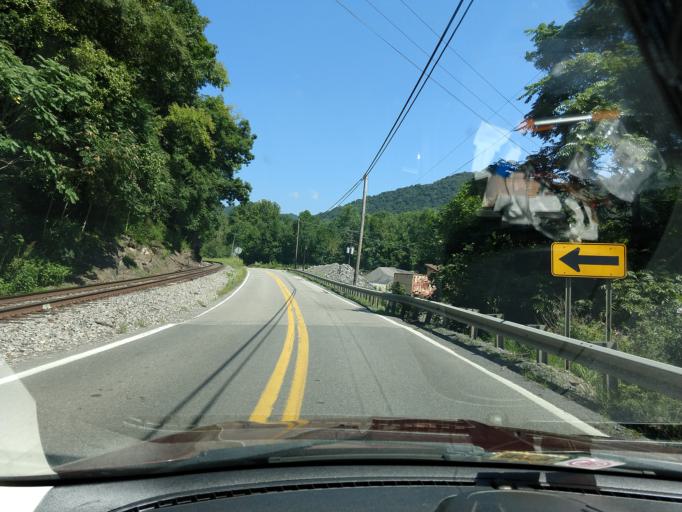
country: US
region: West Virginia
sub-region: Fayette County
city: Ansted
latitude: 38.1417
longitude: -81.2121
